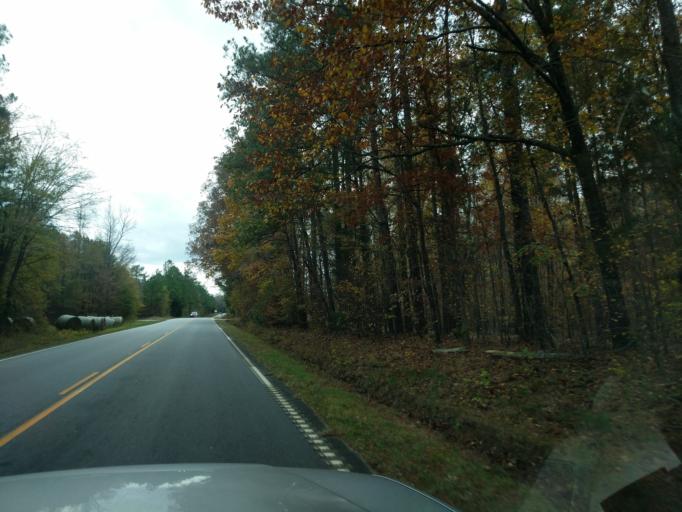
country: US
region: South Carolina
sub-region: Saluda County
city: Saluda
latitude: 34.0665
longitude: -81.8177
